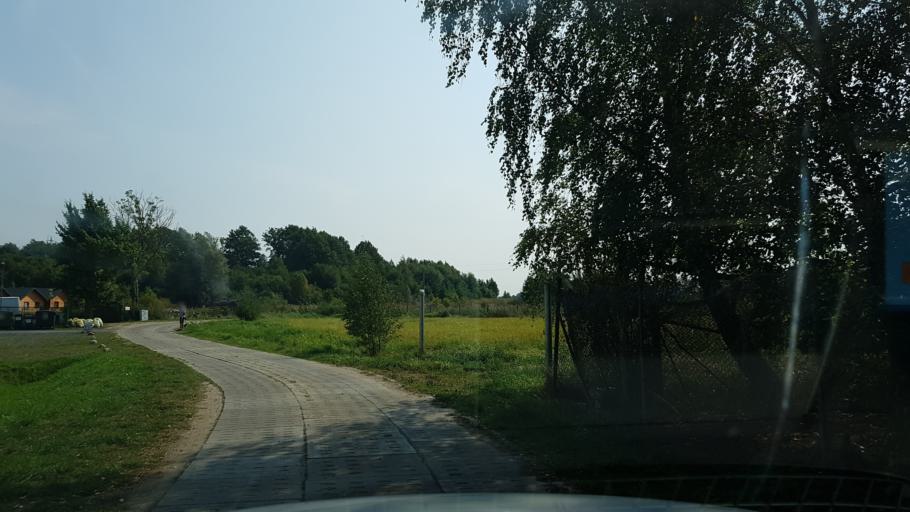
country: PL
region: West Pomeranian Voivodeship
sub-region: Powiat slawienski
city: Darlowo
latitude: 54.5069
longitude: 16.4996
